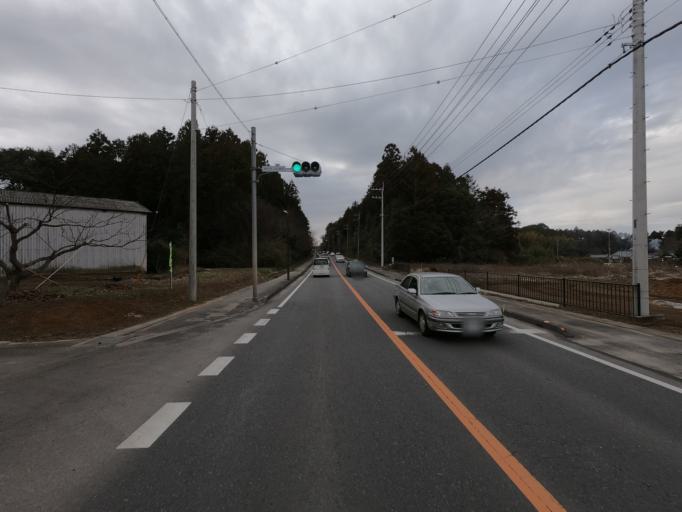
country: JP
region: Ibaraki
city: Ishioka
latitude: 36.0898
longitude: 140.3118
